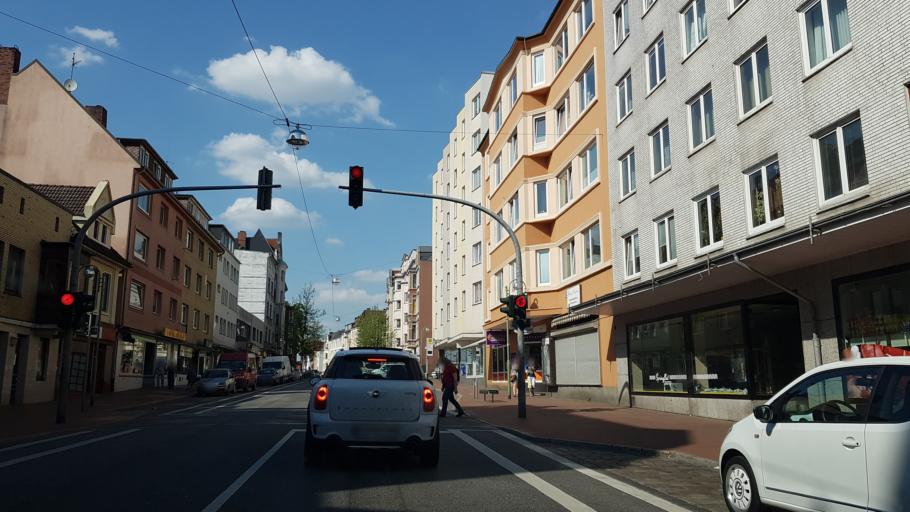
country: DE
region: Bremen
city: Bremerhaven
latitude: 53.5619
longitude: 8.5860
